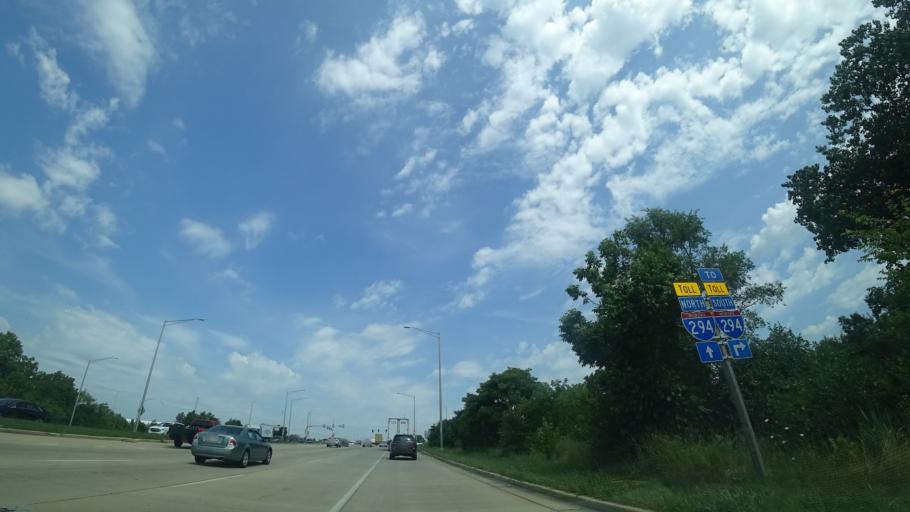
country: US
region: Illinois
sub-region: Cook County
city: Alsip
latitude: 41.6601
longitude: -87.7382
